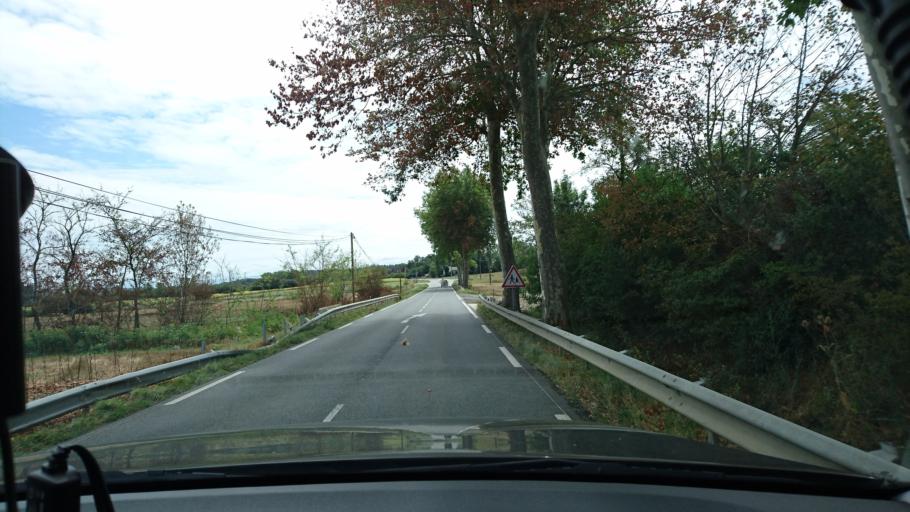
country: FR
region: Midi-Pyrenees
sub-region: Departement de la Haute-Garonne
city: Saint-Sulpice-sur-Leze
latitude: 43.3176
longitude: 1.3231
